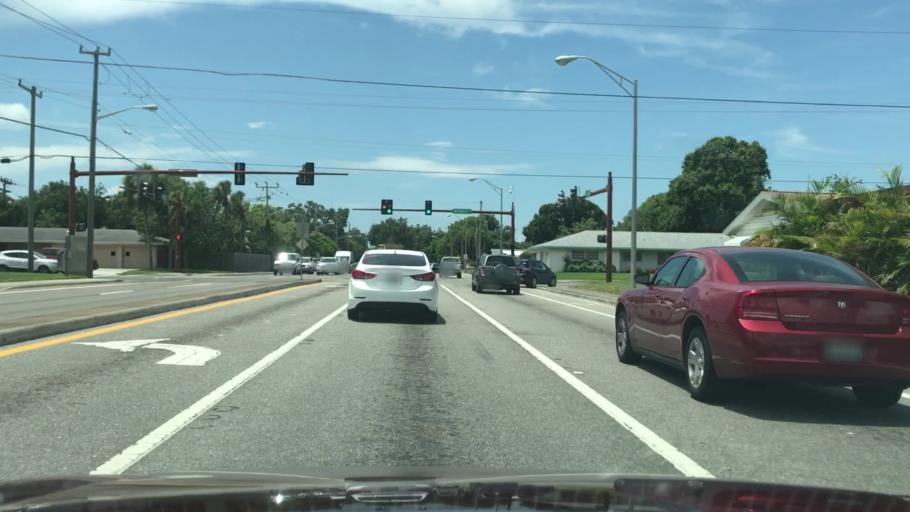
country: US
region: Florida
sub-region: Sarasota County
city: Southgate
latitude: 27.3088
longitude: -82.5142
